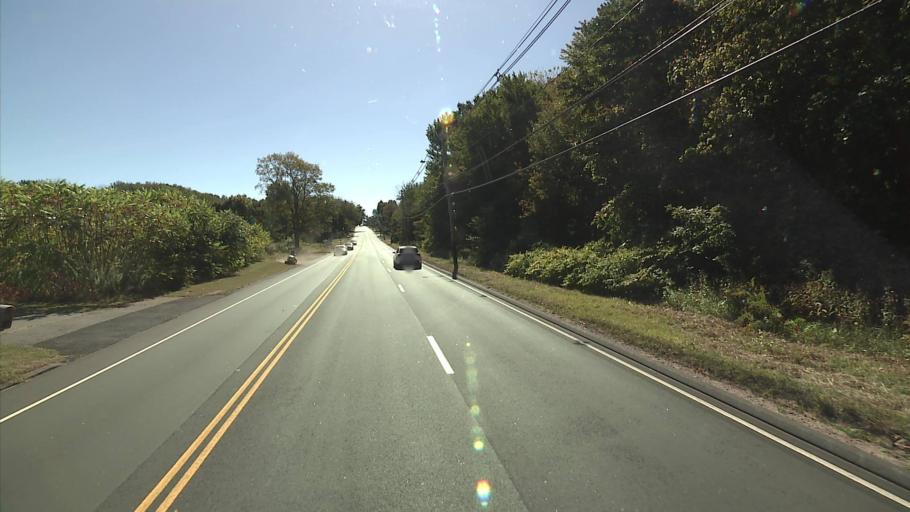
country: US
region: Connecticut
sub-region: New Haven County
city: Prospect
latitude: 41.5206
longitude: -72.9923
